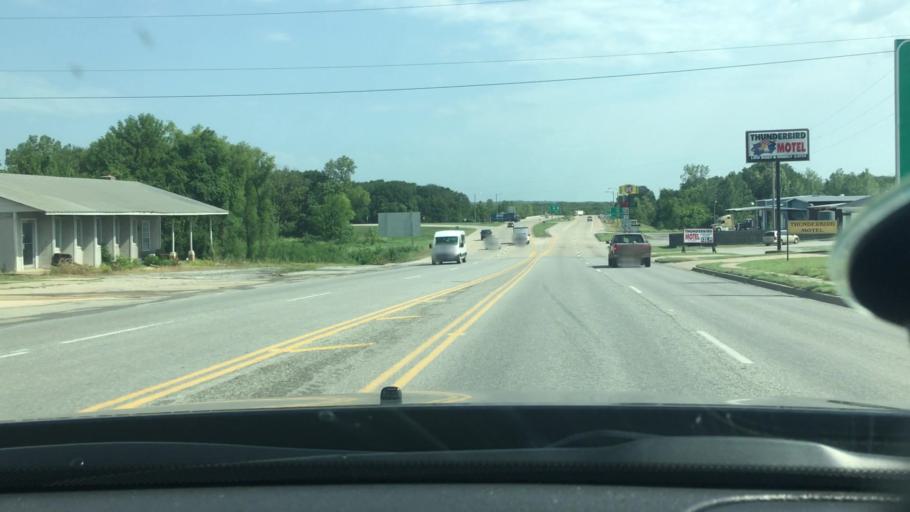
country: US
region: Oklahoma
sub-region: Atoka County
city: Atoka
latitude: 34.3900
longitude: -96.1265
